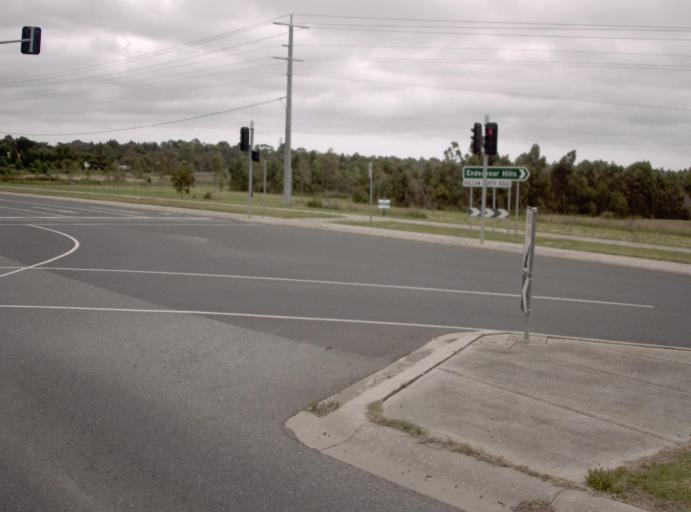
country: AU
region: Victoria
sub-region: Casey
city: Endeavour Hills
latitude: -37.9901
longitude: 145.2765
